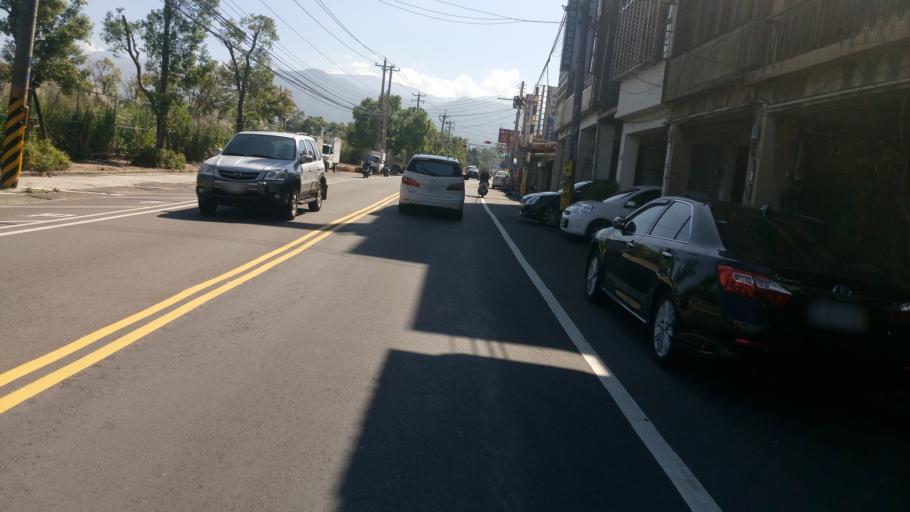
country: TW
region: Taiwan
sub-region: Hsinchu
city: Zhubei
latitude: 24.7287
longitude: 121.0923
